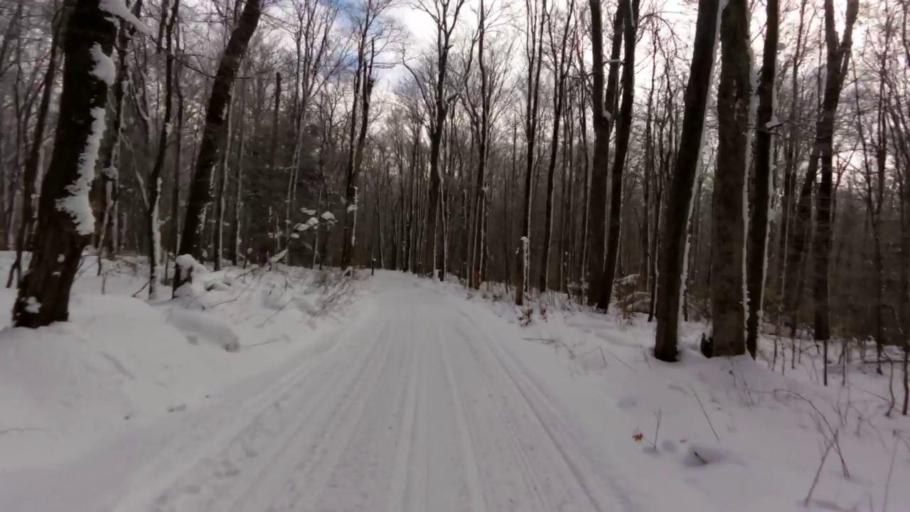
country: US
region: New York
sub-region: Cattaraugus County
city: Salamanca
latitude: 42.0543
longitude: -78.7675
